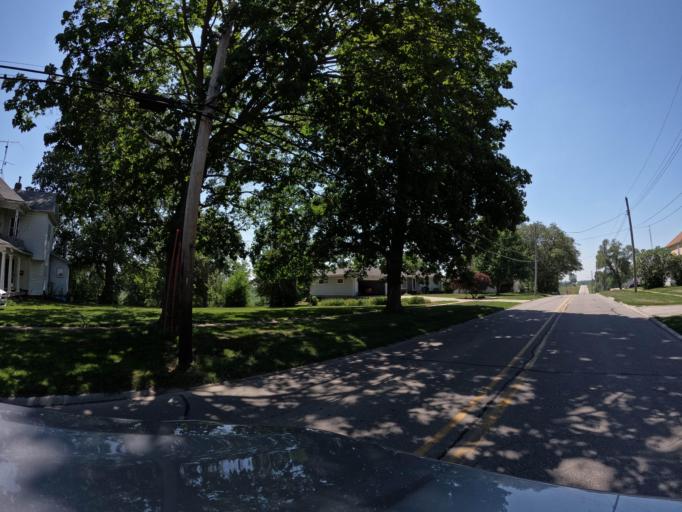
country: US
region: Iowa
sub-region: Keokuk County
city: Sigourney
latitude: 41.3245
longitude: -92.2052
